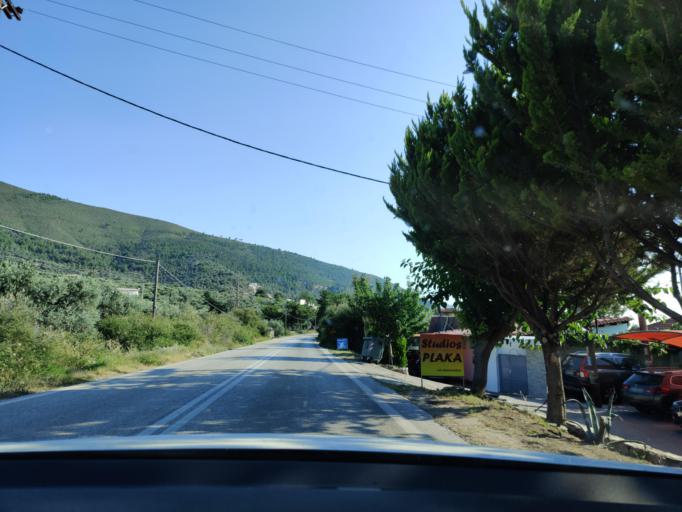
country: GR
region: East Macedonia and Thrace
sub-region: Nomos Kavalas
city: Prinos
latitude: 40.6872
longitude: 24.5265
